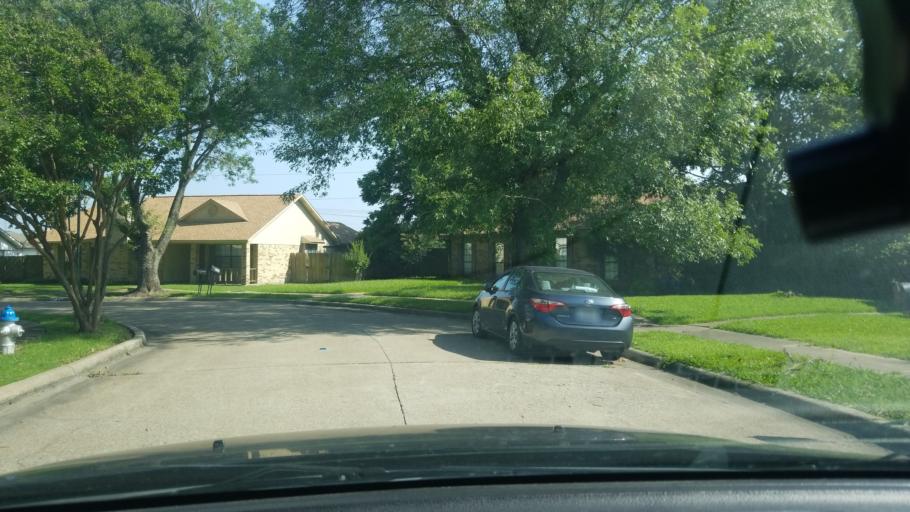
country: US
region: Texas
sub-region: Dallas County
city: Mesquite
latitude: 32.8204
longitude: -96.6150
